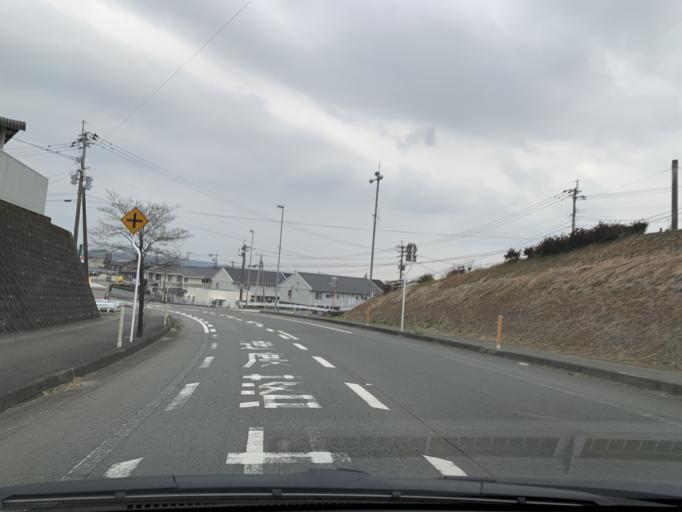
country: JP
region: Kumamoto
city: Ozu
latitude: 32.8816
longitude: 130.8773
